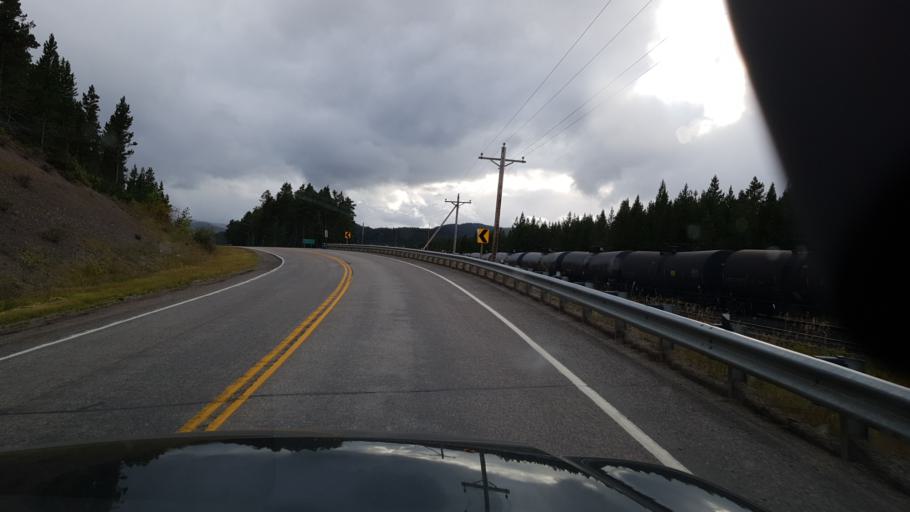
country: US
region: Montana
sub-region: Glacier County
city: South Browning
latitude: 48.3234
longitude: -113.3479
